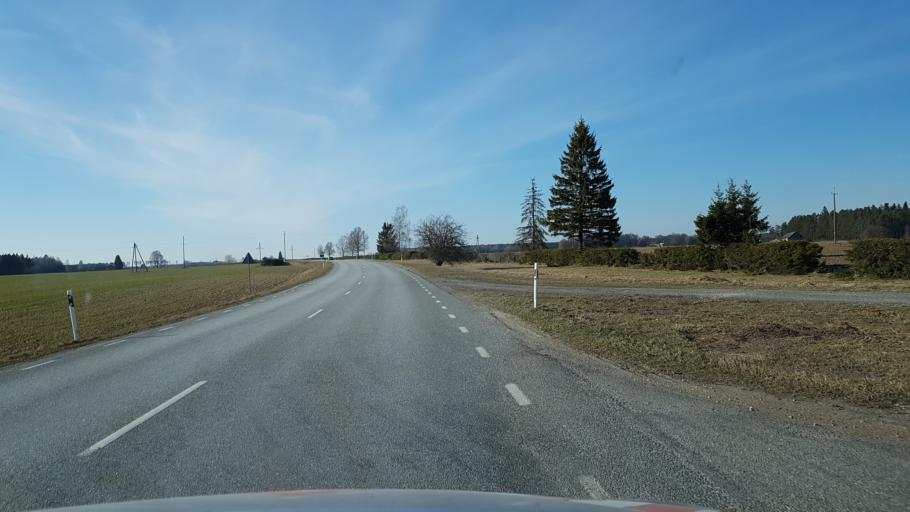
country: EE
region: Laeaene-Virumaa
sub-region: Vinni vald
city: Vinni
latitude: 59.2077
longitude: 26.5538
